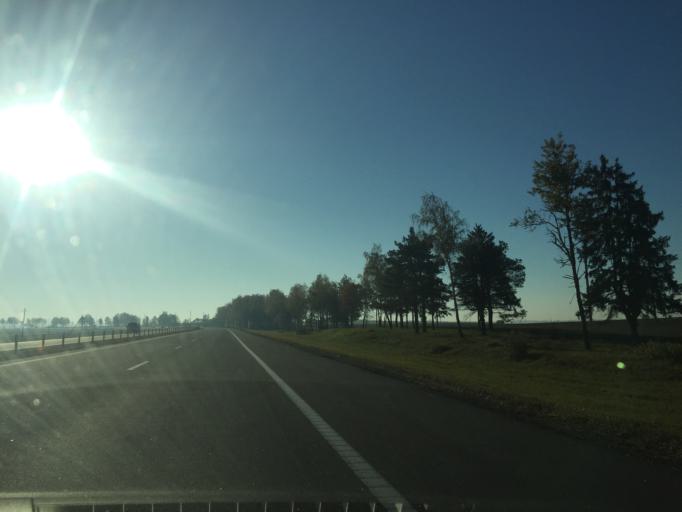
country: BY
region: Minsk
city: Luhavaya Slabada
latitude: 53.7685
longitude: 27.8631
